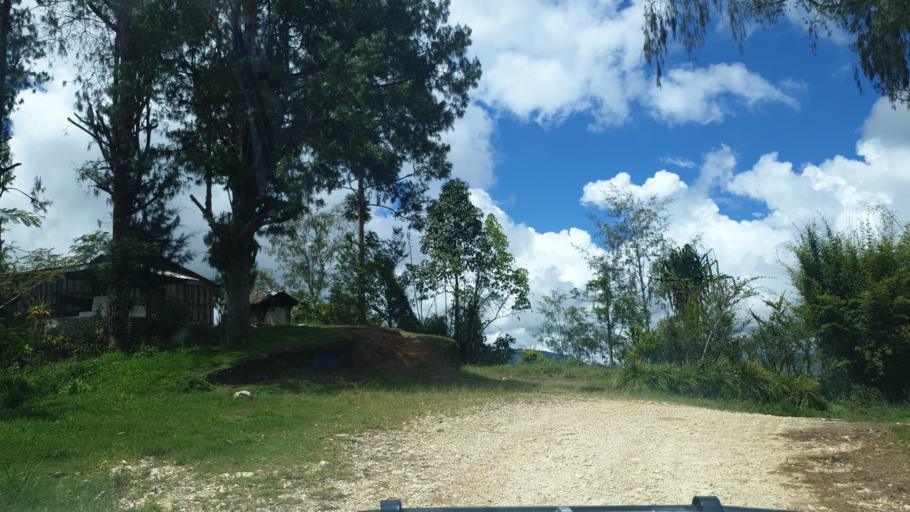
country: PG
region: Chimbu
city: Kundiawa
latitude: -6.2191
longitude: 145.1378
